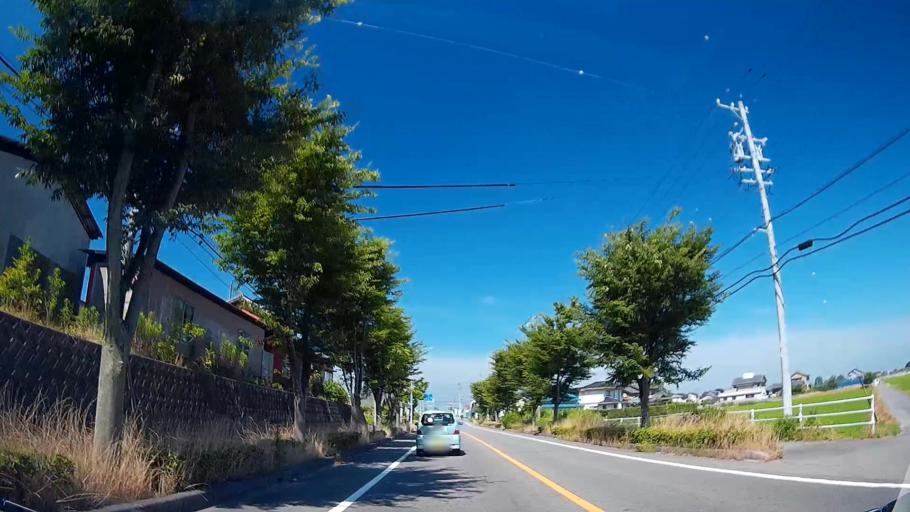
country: JP
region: Aichi
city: Nishio
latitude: 34.8256
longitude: 137.0893
